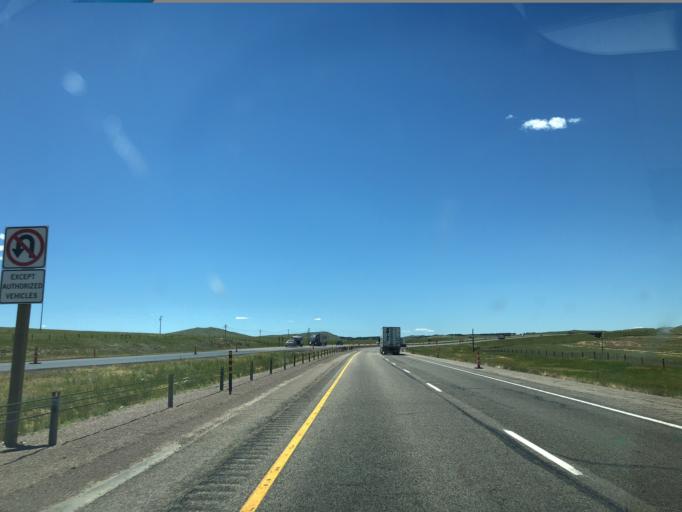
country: US
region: Wyoming
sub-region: Laramie County
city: Cheyenne
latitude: 41.0957
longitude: -105.1953
